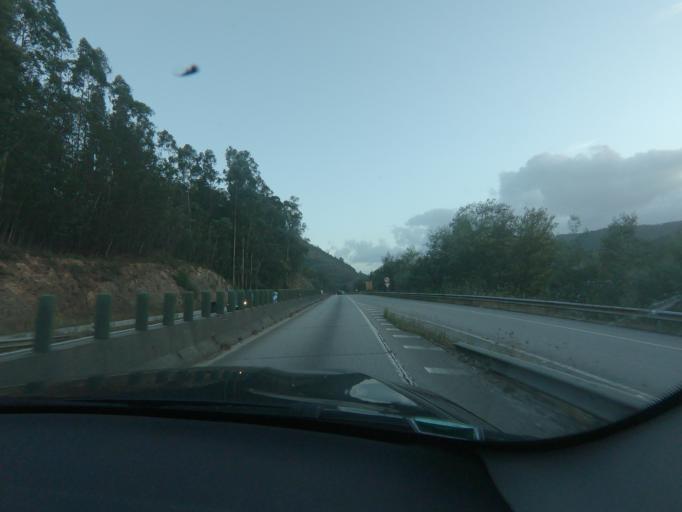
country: PT
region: Coimbra
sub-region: Penacova
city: Penacova
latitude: 40.2930
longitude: -8.2555
